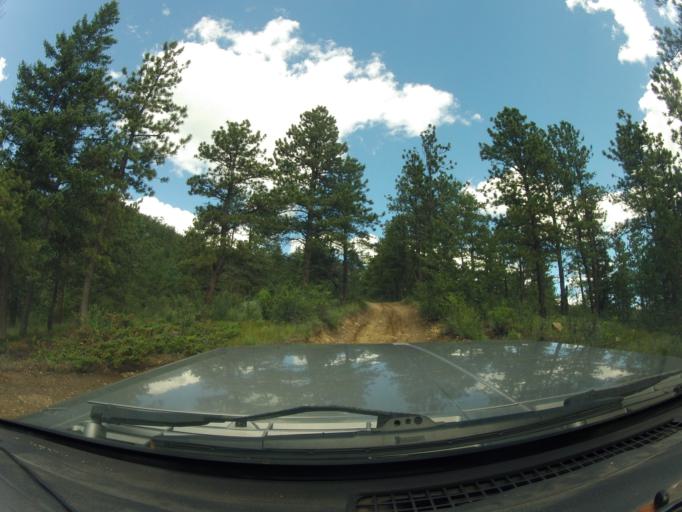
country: US
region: Colorado
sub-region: Larimer County
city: Laporte
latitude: 40.5700
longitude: -105.3503
